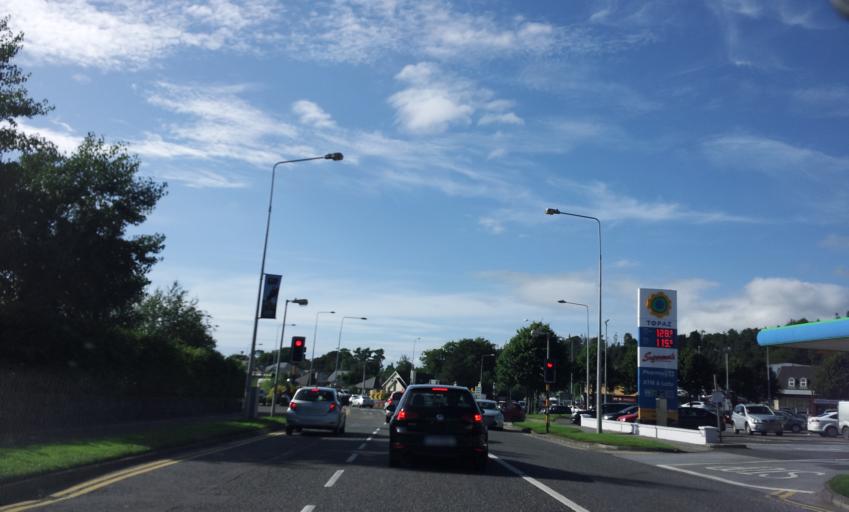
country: IE
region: Munster
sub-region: Ciarrai
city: Cill Airne
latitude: 52.0597
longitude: -9.4819
